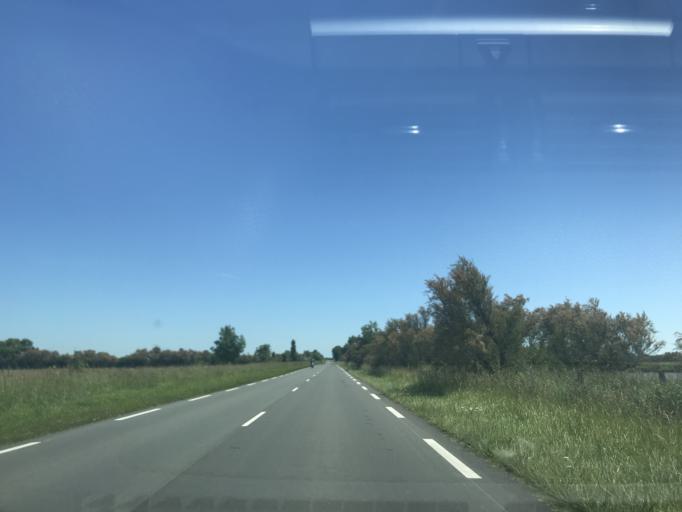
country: FR
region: Poitou-Charentes
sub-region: Departement de la Charente-Maritime
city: Meschers-sur-Gironde
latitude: 45.5569
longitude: -0.9254
